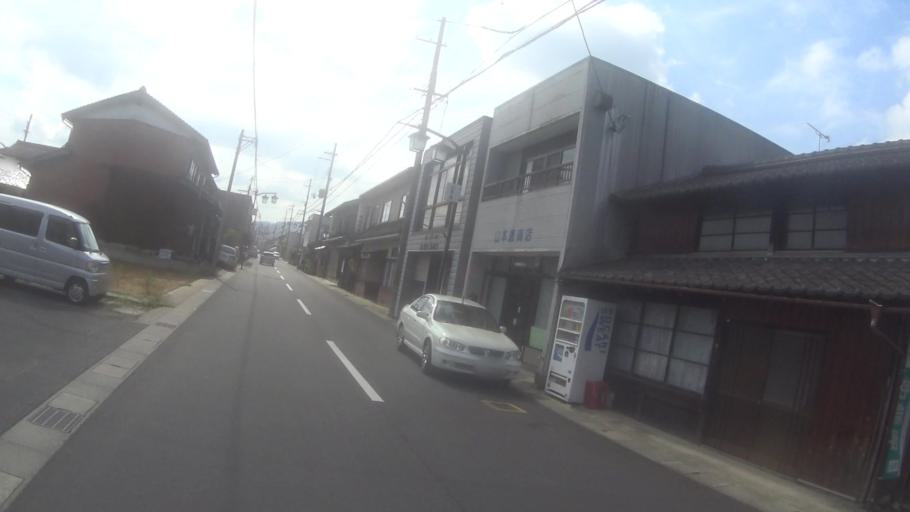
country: JP
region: Kyoto
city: Miyazu
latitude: 35.5806
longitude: 135.0931
